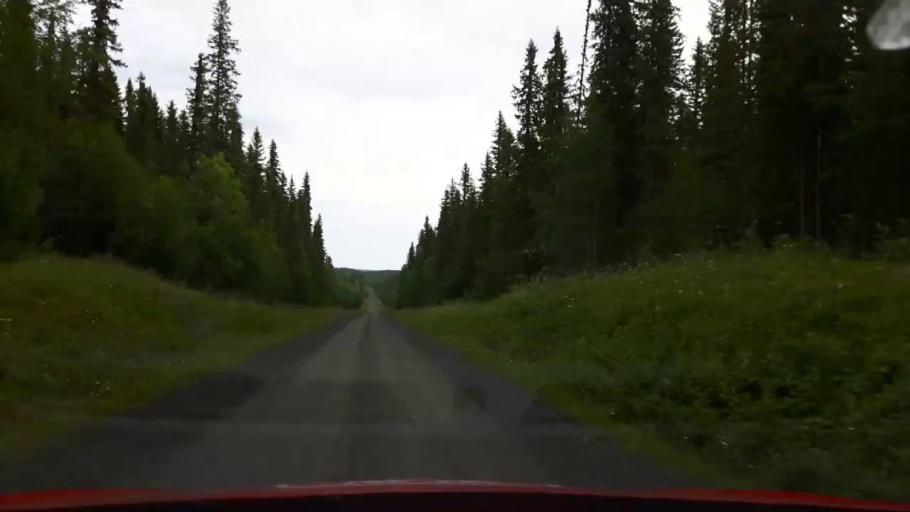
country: SE
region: Jaemtland
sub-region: OEstersunds Kommun
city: Lit
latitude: 63.3915
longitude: 15.2139
